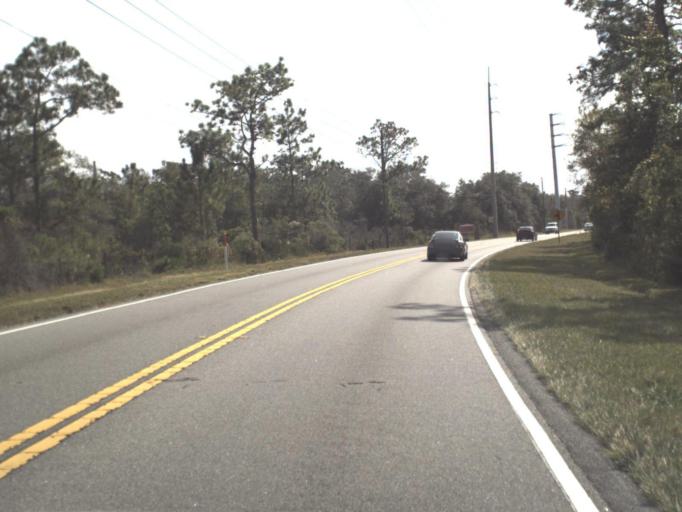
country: US
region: Florida
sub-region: Osceola County
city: Poinciana
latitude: 28.1956
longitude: -81.4695
